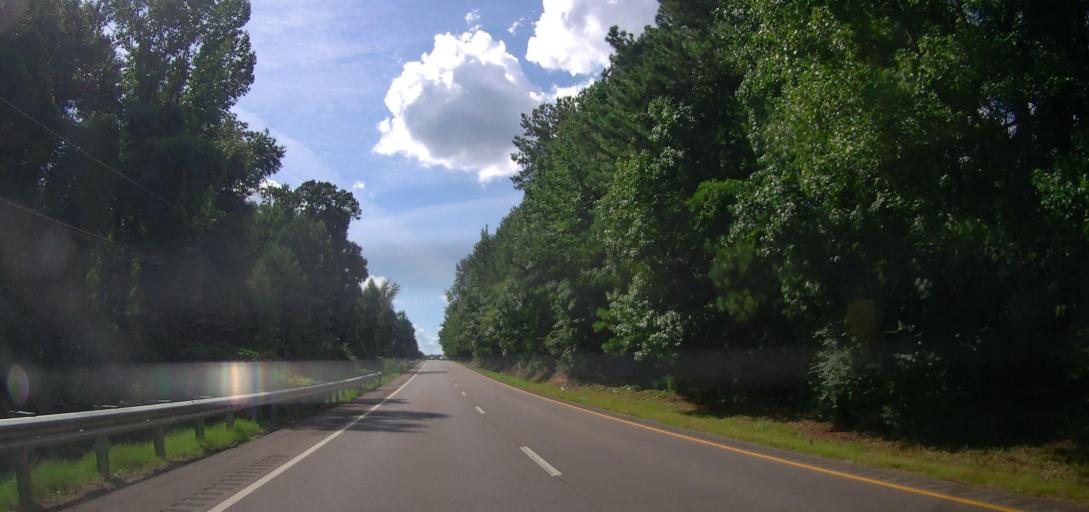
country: US
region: Alabama
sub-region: Tuscaloosa County
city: Northport
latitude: 33.2416
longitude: -87.6648
